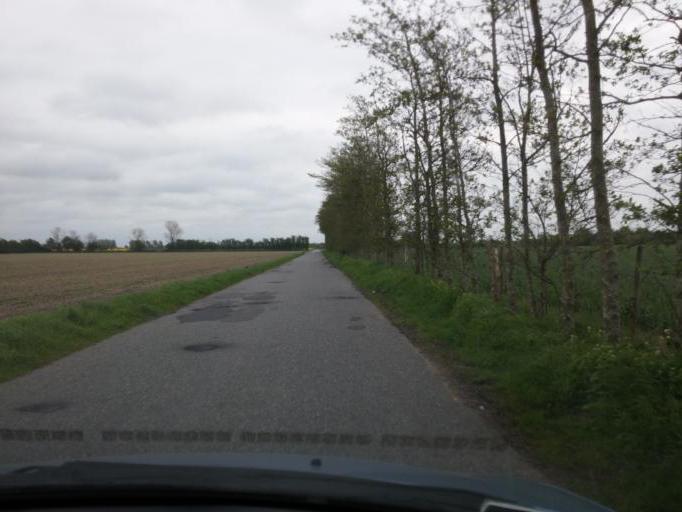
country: DK
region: South Denmark
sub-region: Odense Kommune
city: Bullerup
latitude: 55.4080
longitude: 10.5157
